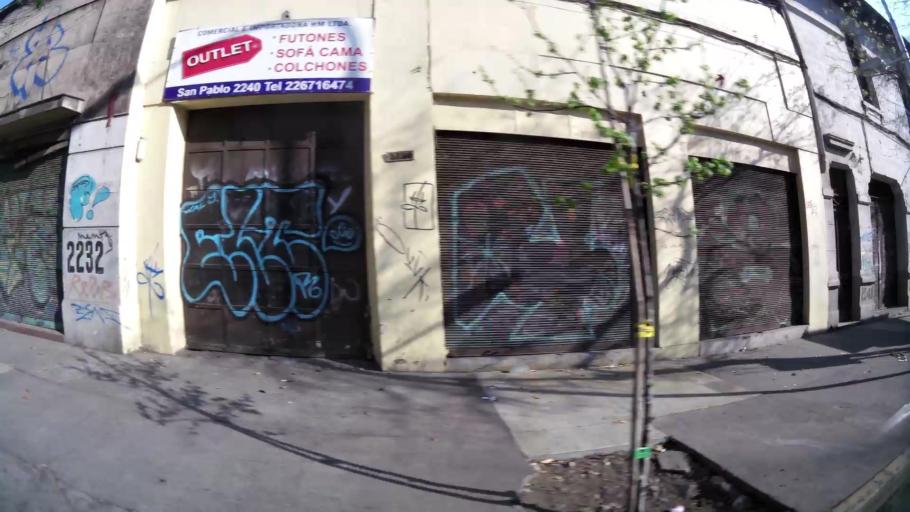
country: CL
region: Santiago Metropolitan
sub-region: Provincia de Santiago
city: Santiago
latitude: -33.4350
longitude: -70.6680
